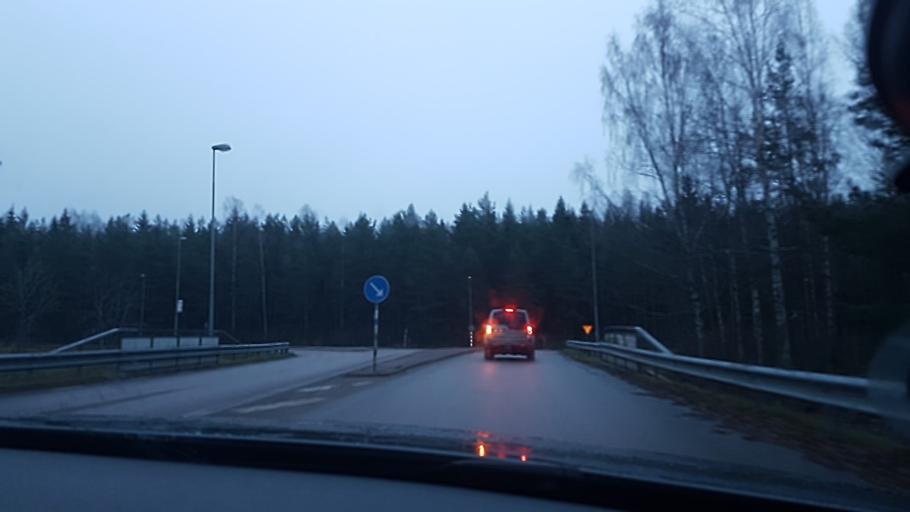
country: SE
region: Vaermland
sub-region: Kristinehamns Kommun
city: Kristinehamn
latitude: 59.3107
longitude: 14.1415
